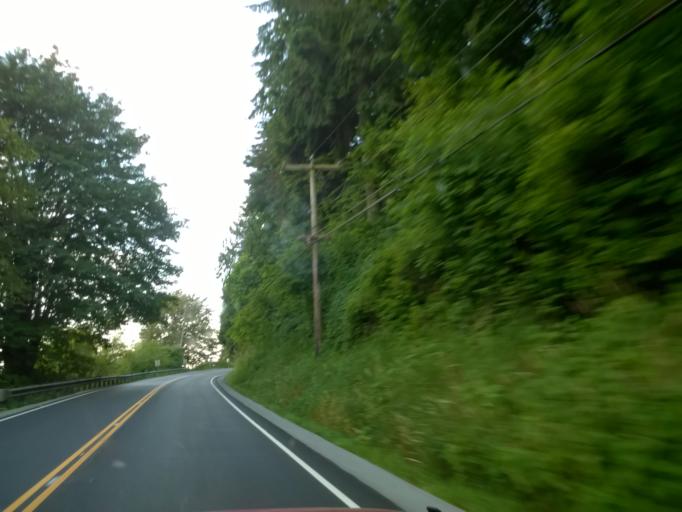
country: US
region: Washington
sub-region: King County
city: Duvall
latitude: 47.7295
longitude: -122.0104
